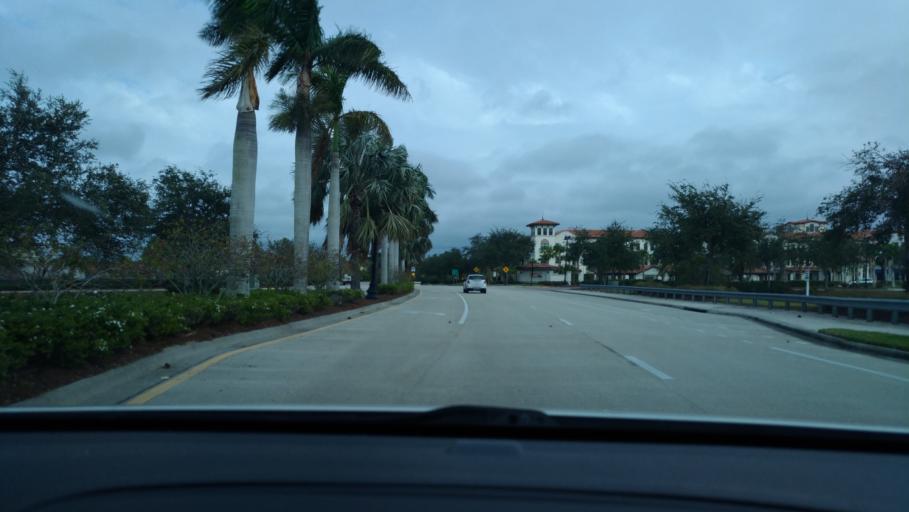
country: US
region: Florida
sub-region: Lee County
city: Estero
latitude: 26.3928
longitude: -81.8084
